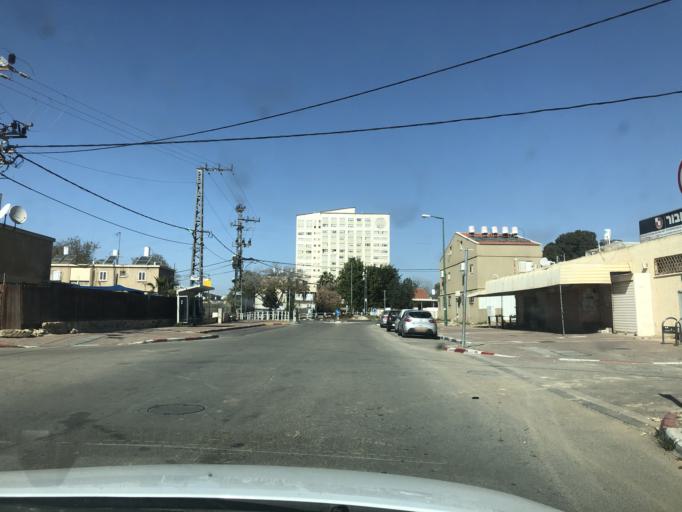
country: IL
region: Southern District
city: Beersheba
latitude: 31.2612
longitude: 34.7951
